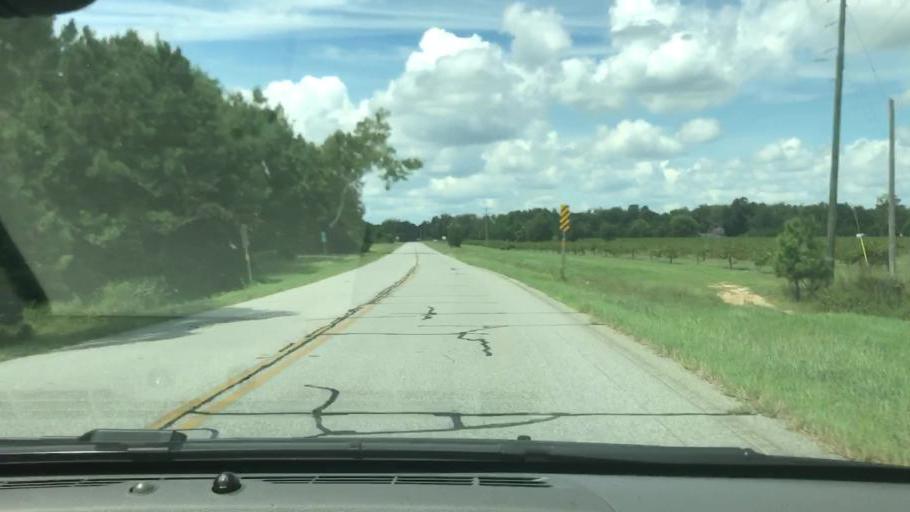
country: US
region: Georgia
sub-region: Stewart County
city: Lumpkin
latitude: 32.1402
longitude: -85.0047
